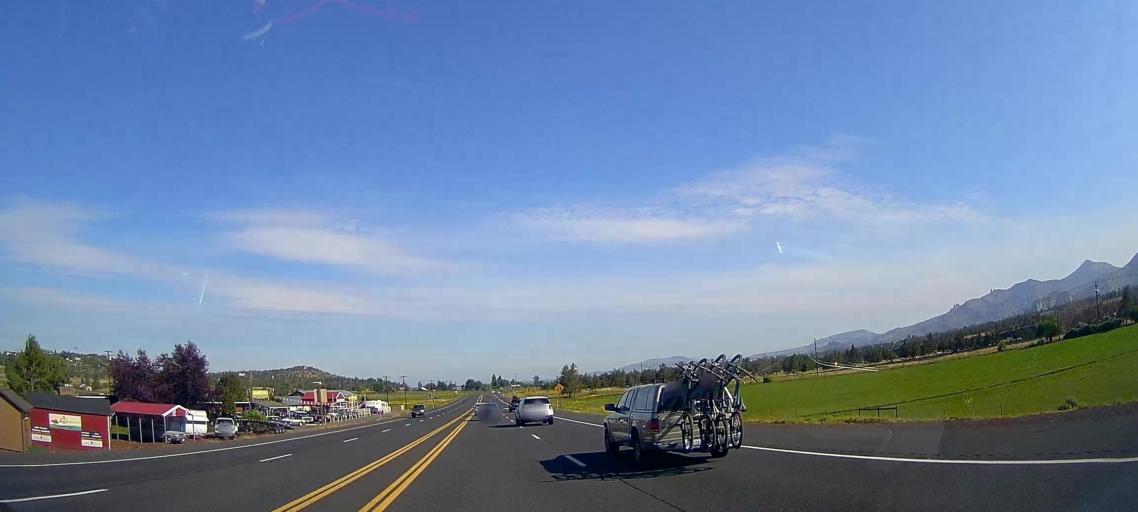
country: US
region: Oregon
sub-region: Deschutes County
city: Terrebonne
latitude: 44.3205
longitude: -121.1726
